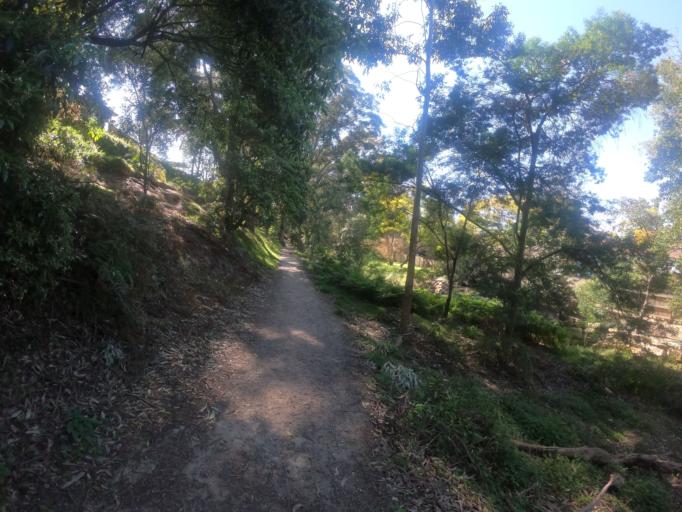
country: AU
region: New South Wales
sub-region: Ryde
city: East Ryde
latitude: -33.8148
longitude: 151.1149
